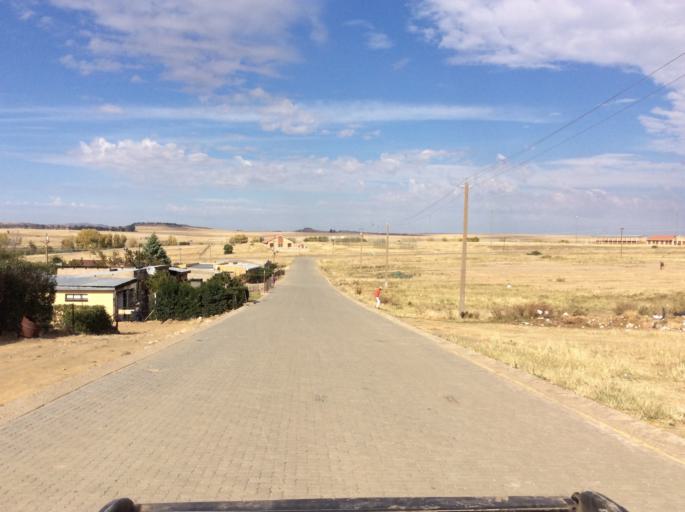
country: LS
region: Mafeteng
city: Mafeteng
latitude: -29.7195
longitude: 27.0170
